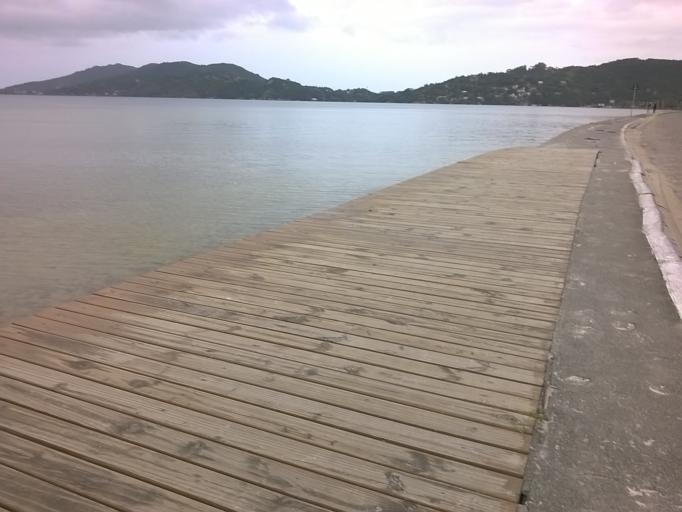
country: BR
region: Santa Catarina
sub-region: Florianopolis
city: Lagoa
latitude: -27.6080
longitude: -48.4558
